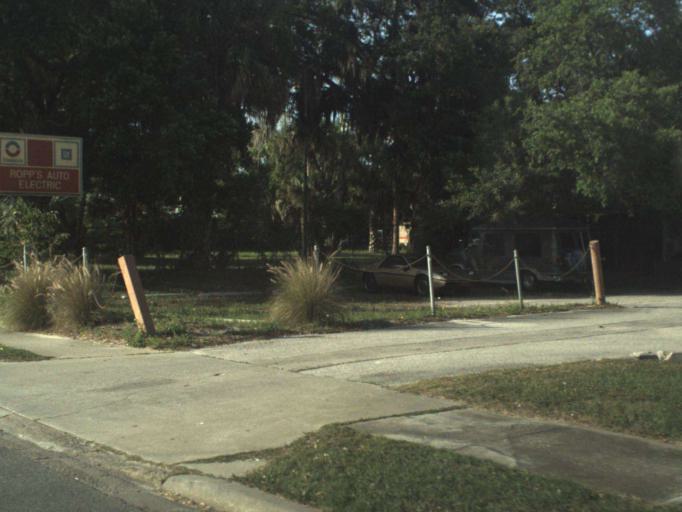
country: US
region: Florida
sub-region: Volusia County
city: New Smyrna Beach
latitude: 29.0264
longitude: -80.9275
